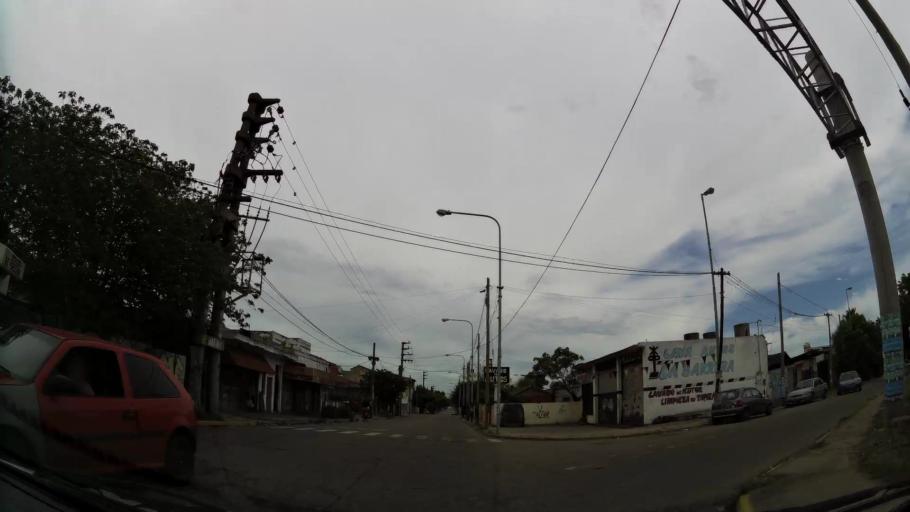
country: AR
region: Buenos Aires
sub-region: Partido de Quilmes
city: Quilmes
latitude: -34.7582
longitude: -58.2211
